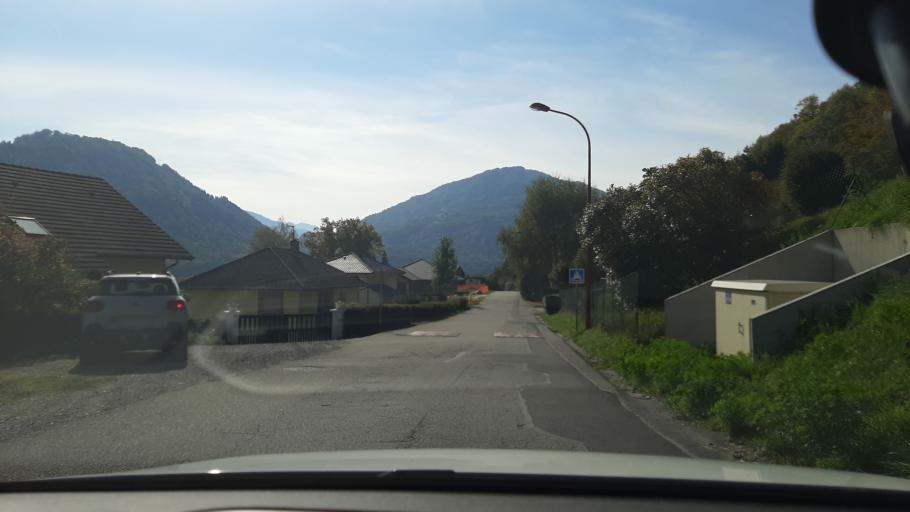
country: FR
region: Rhone-Alpes
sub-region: Departement de la Savoie
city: La Rochette
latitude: 45.4595
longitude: 6.1069
